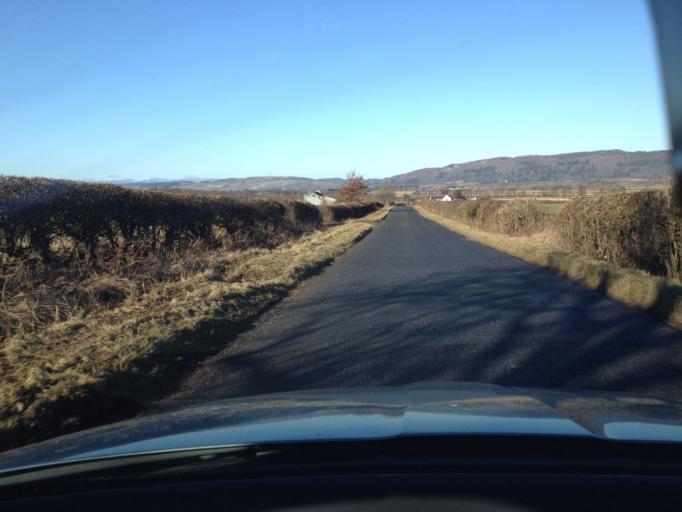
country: GB
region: Scotland
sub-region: Perth and Kinross
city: Bridge of Earn
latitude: 56.3224
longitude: -3.3736
